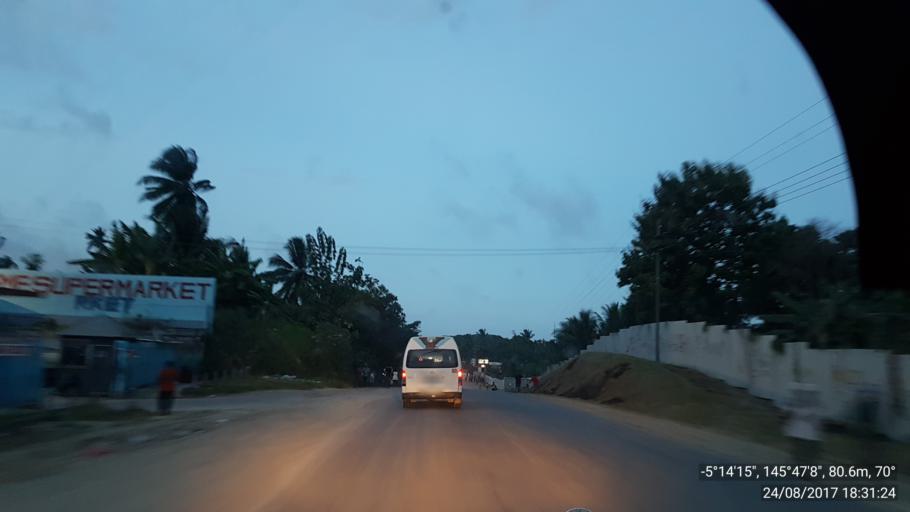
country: PG
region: Madang
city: Madang
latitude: -5.2375
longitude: 145.7858
